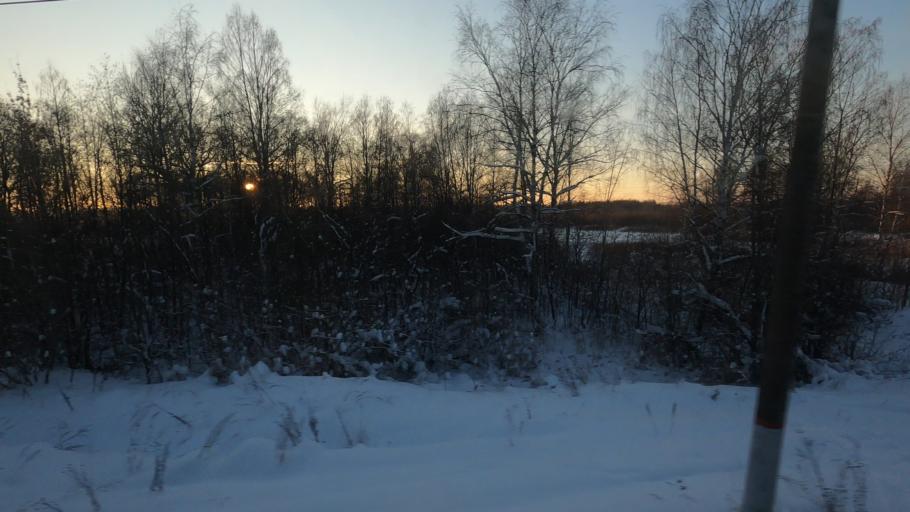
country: RU
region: Moskovskaya
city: Dmitrov
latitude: 56.3800
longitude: 37.5191
